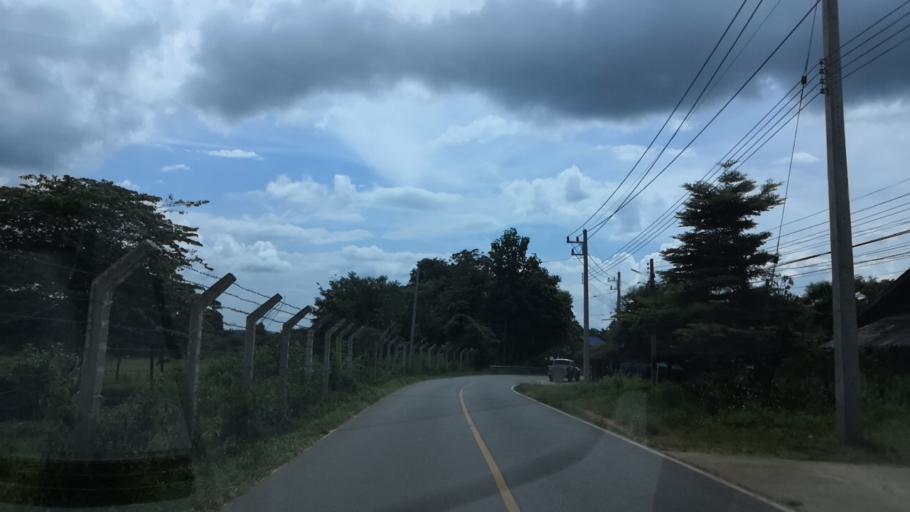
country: TH
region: Mae Hong Son
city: Khun Yuam
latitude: 18.8240
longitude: 97.9301
